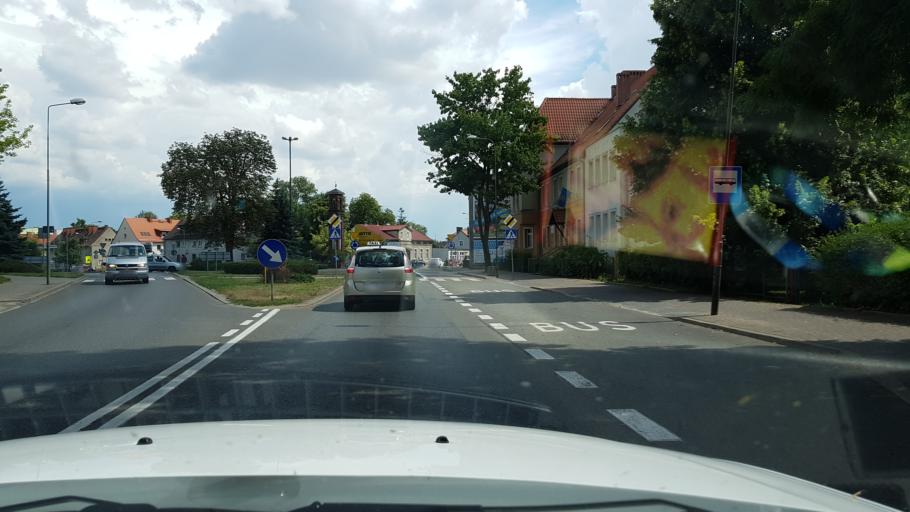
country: PL
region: West Pomeranian Voivodeship
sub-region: Powiat walecki
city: Walcz
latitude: 53.2773
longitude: 16.4623
